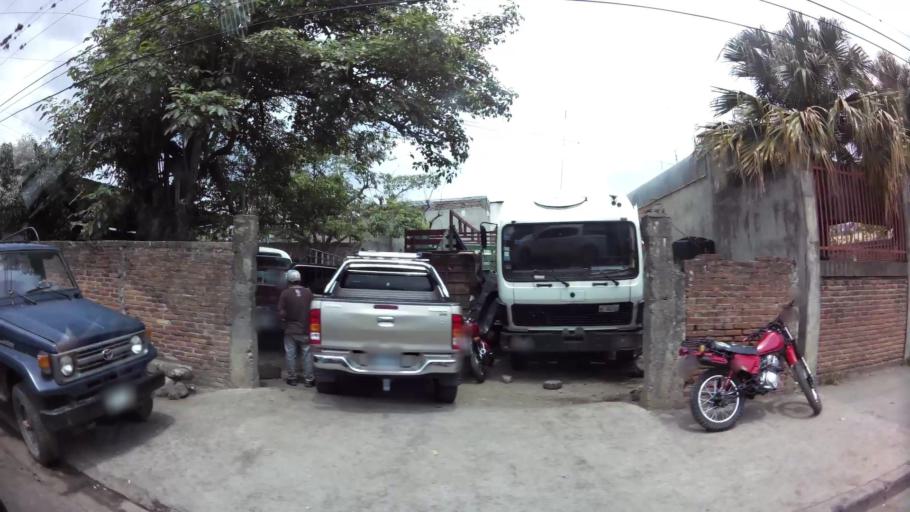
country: NI
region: Matagalpa
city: Matagalpa
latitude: 12.9290
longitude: -85.9129
